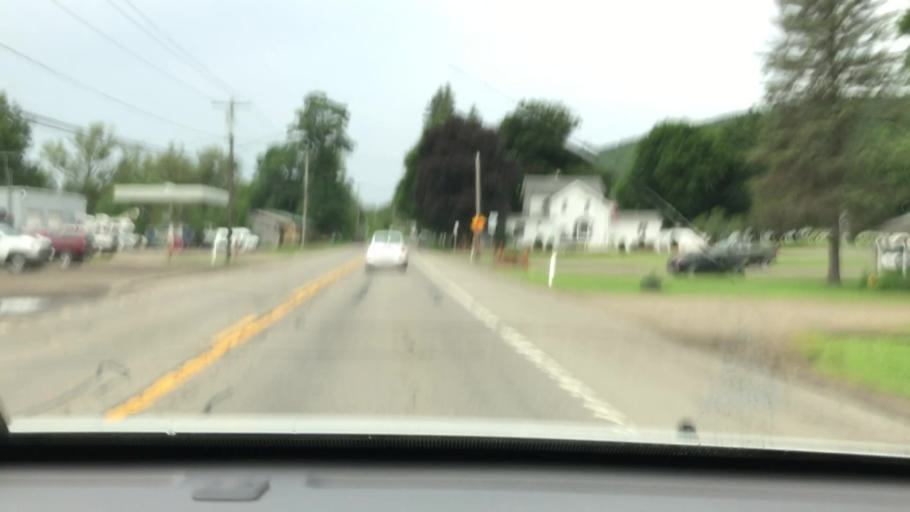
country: US
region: New York
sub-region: Cattaraugus County
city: Salamanca
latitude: 42.2127
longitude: -78.6381
